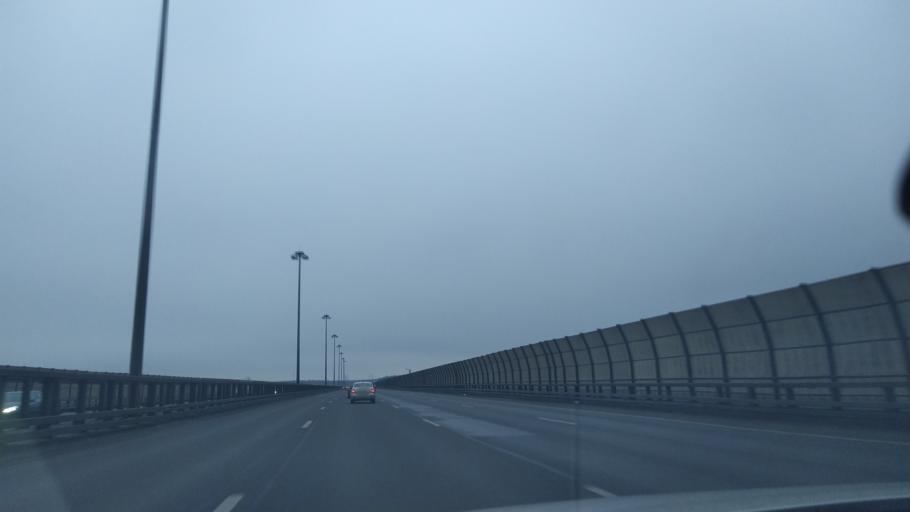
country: RU
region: St.-Petersburg
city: Krasnogvargeisky
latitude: 59.9795
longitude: 30.5242
